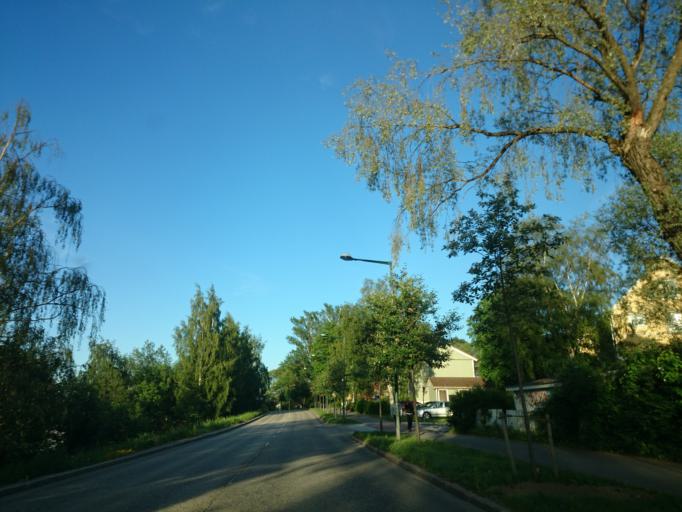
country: SE
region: Vaesternorrland
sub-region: Sundsvalls Kommun
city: Sundsvall
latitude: 62.3845
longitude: 17.3171
